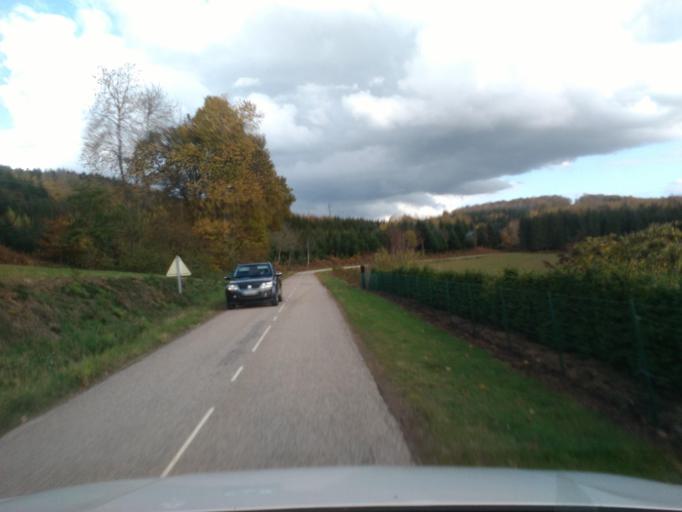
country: FR
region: Lorraine
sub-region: Departement des Vosges
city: Senones
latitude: 48.3703
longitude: 7.0095
